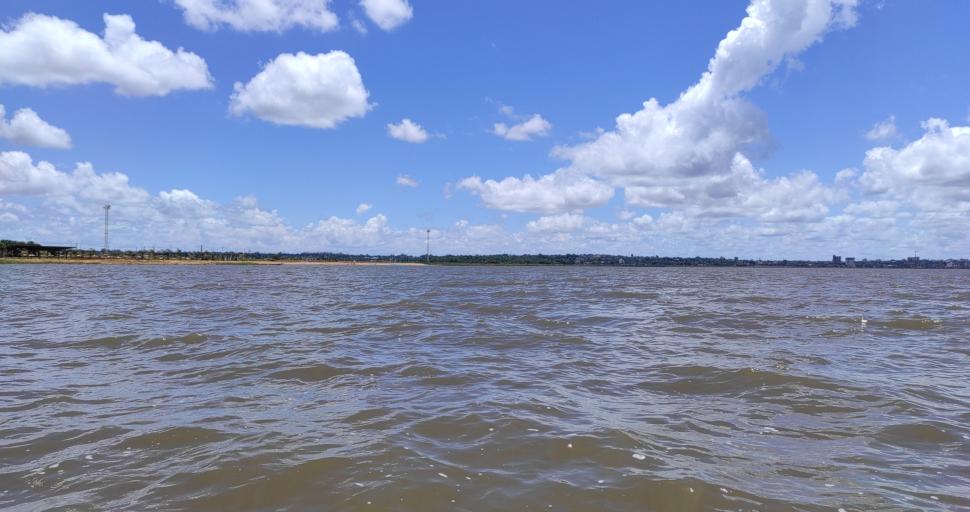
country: AR
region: Misiones
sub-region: Departamento de Capital
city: Posadas
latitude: -27.4193
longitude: -55.8744
